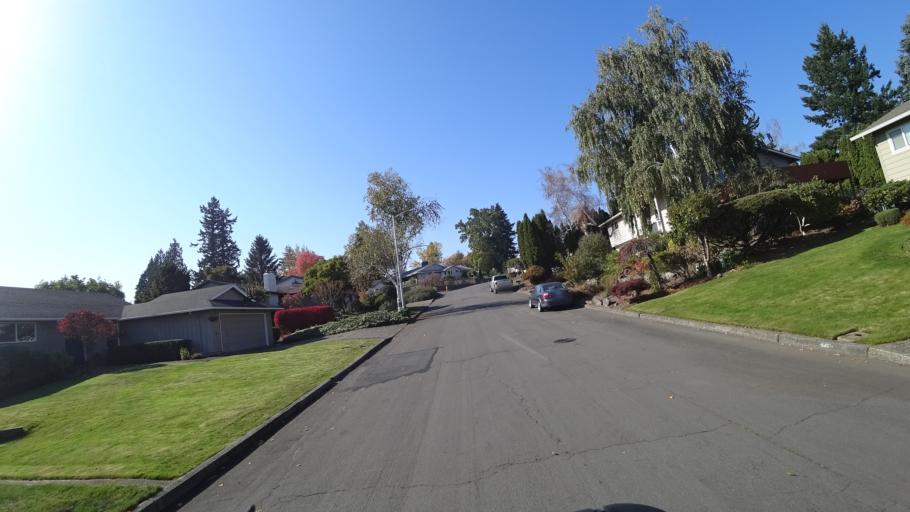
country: US
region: Oregon
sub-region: Multnomah County
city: Gresham
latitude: 45.4997
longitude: -122.4418
